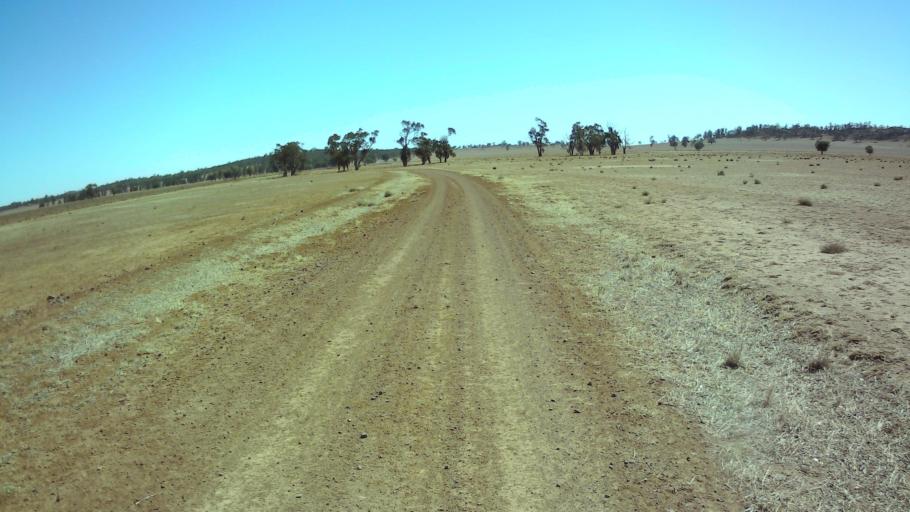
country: AU
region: New South Wales
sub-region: Forbes
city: Forbes
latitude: -33.7006
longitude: 147.6695
